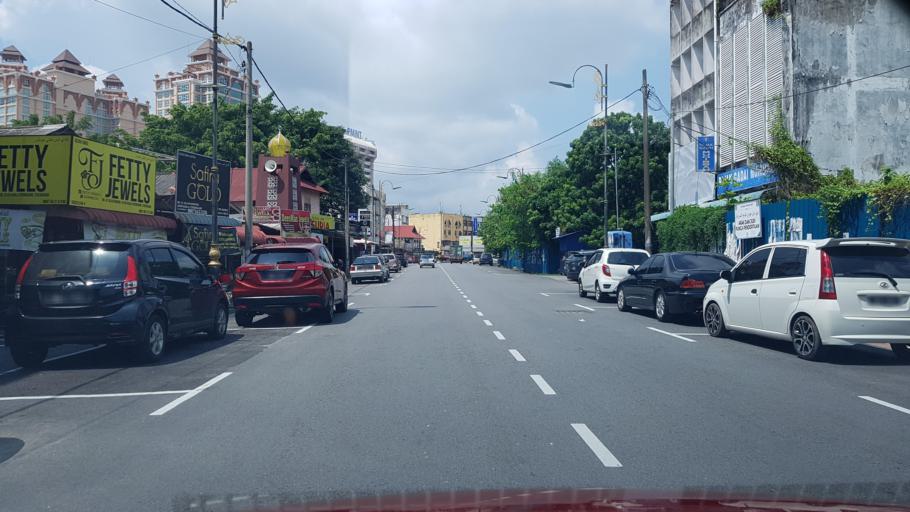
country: MY
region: Terengganu
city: Kuala Terengganu
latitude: 5.3337
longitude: 103.1353
